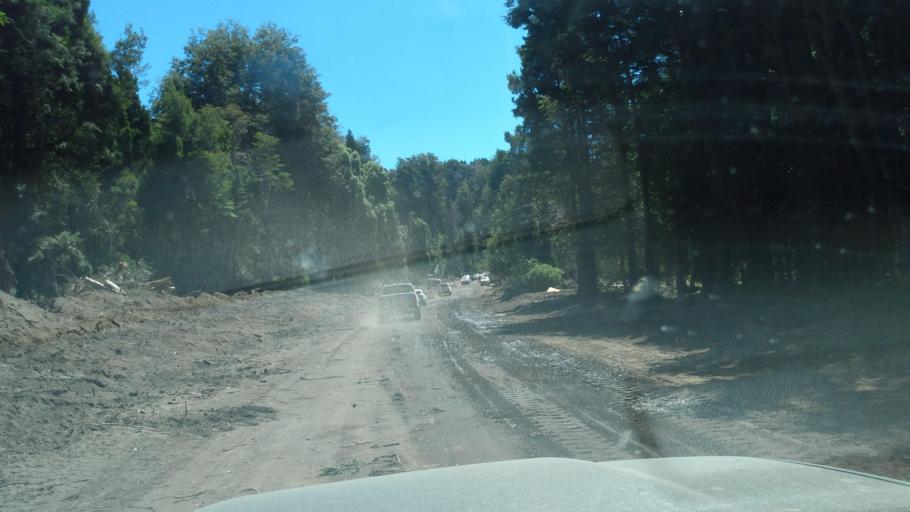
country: AR
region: Neuquen
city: Villa La Angostura
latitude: -40.6267
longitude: -71.4974
